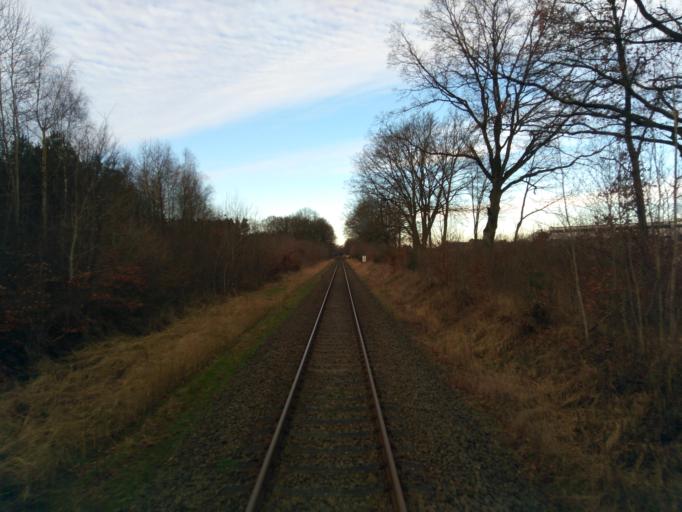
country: DE
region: Lower Saxony
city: Uelzen
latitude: 52.9909
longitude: 10.5305
